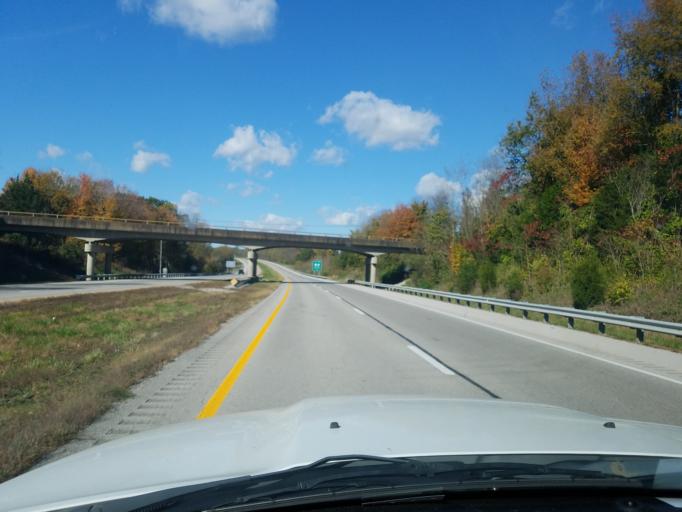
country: US
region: Kentucky
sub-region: Barren County
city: Glasgow
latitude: 36.9883
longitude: -85.9545
